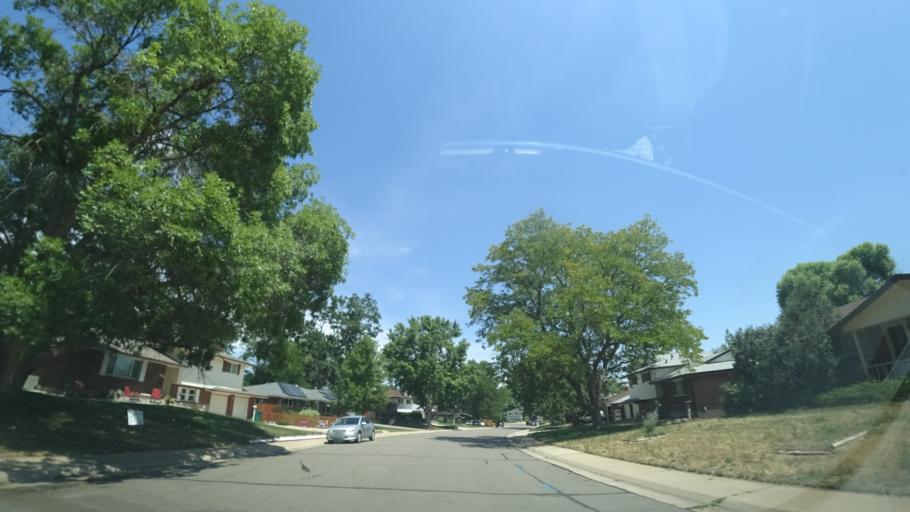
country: US
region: Colorado
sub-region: Jefferson County
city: Lakewood
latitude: 39.6939
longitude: -105.0915
